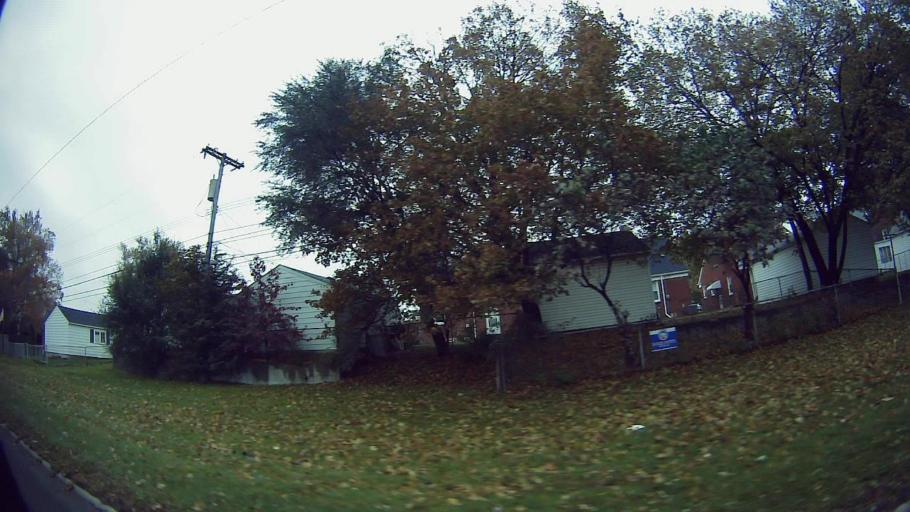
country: US
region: Michigan
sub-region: Wayne County
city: Dearborn Heights
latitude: 42.3189
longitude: -83.2725
